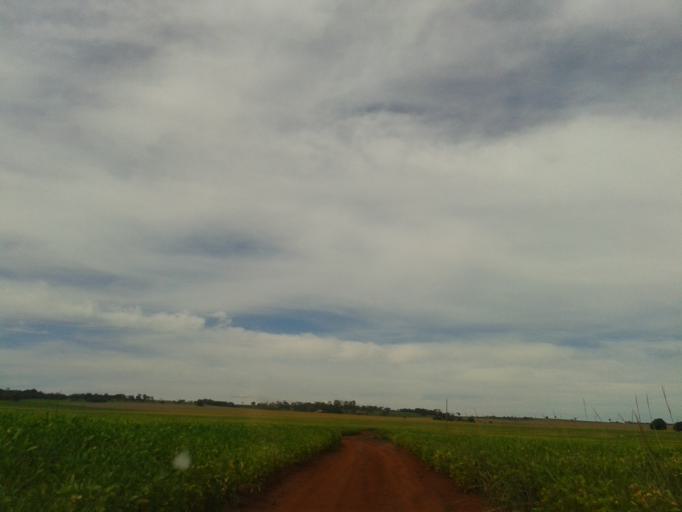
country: BR
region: Minas Gerais
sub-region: Capinopolis
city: Capinopolis
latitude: -18.7742
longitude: -49.8022
